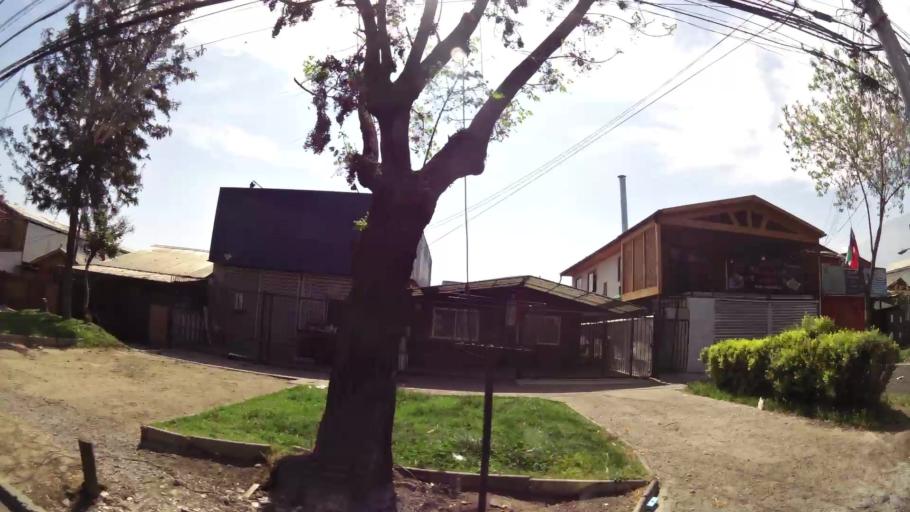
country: CL
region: Santiago Metropolitan
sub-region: Provincia de Santiago
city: Villa Presidente Frei, Nunoa, Santiago, Chile
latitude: -33.4706
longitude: -70.5471
